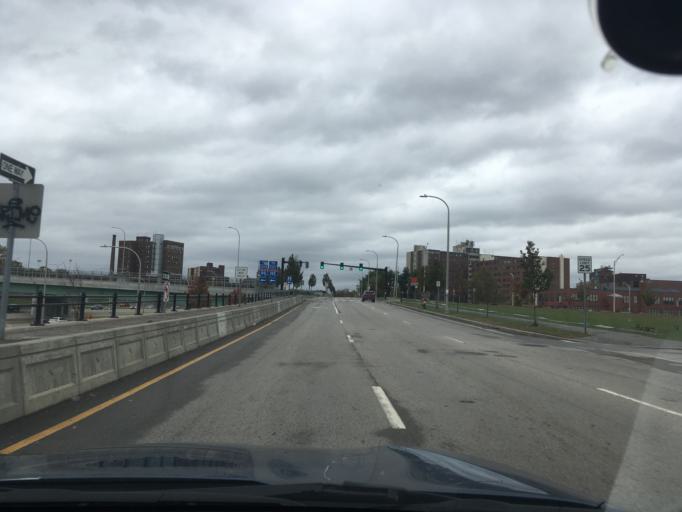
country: US
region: Rhode Island
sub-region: Providence County
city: Providence
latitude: 41.8159
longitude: -71.4127
